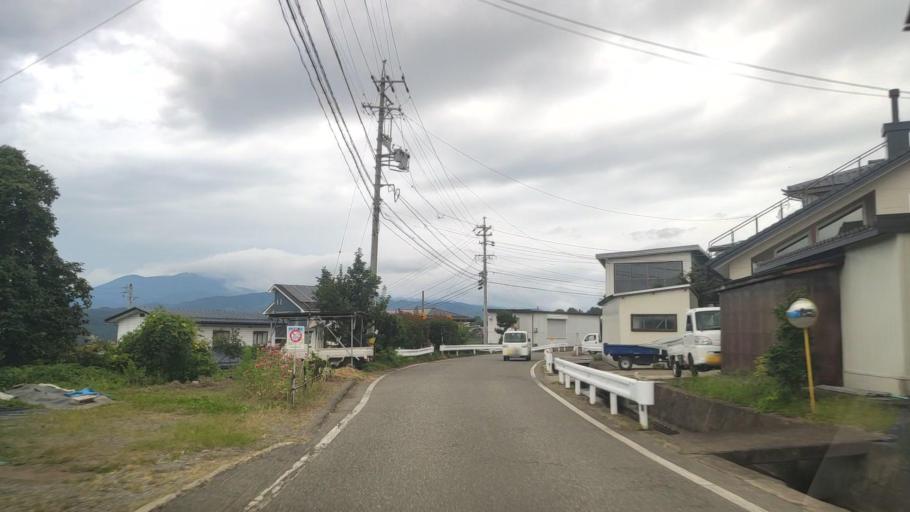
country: JP
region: Nagano
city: Nakano
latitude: 36.7767
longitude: 138.3753
